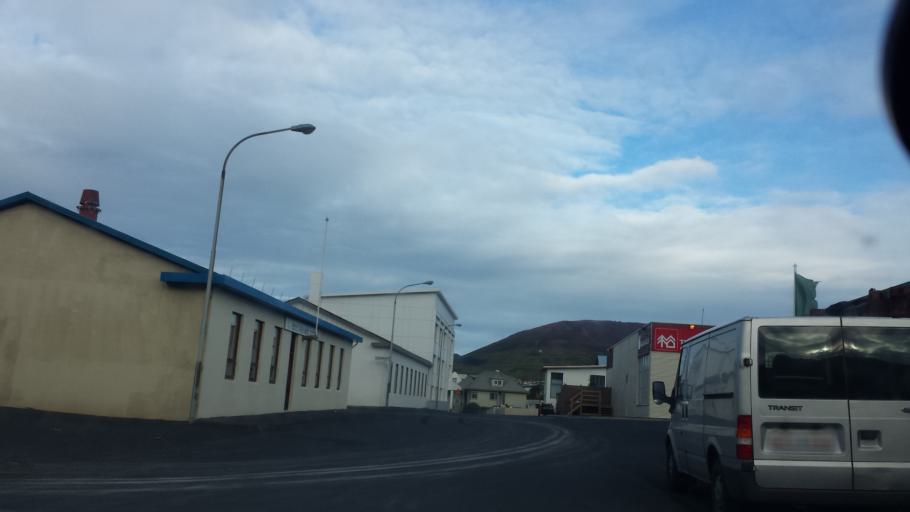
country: IS
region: South
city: Vestmannaeyjar
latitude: 63.4420
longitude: -20.2771
